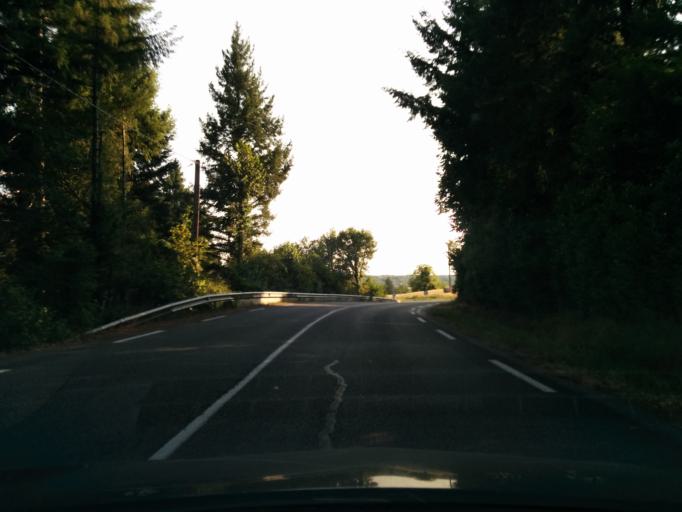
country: FR
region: Midi-Pyrenees
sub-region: Departement du Lot
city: Le Vigan
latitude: 44.7875
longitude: 1.4697
